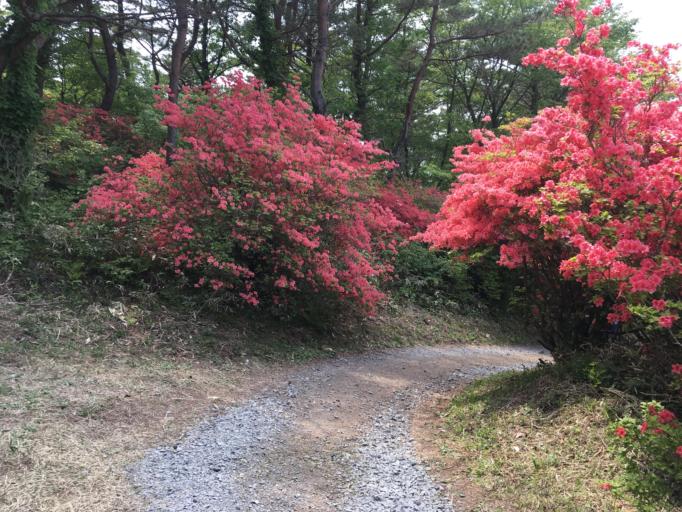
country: JP
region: Iwate
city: Ofunato
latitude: 38.8530
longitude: 141.4711
